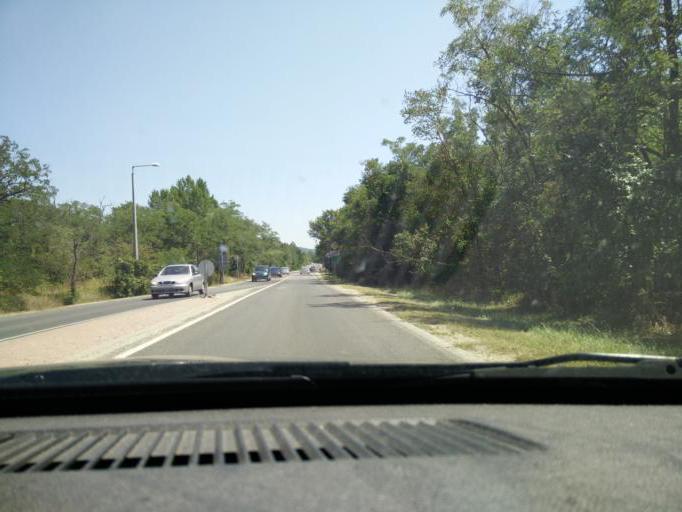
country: HU
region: Komarom-Esztergom
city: Baj
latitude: 47.6352
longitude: 18.3519
